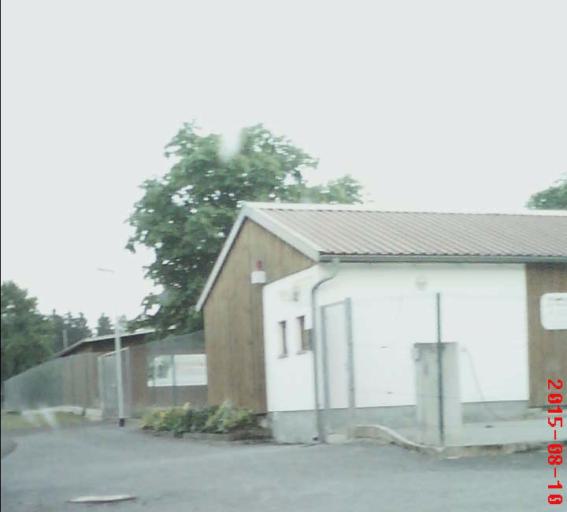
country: DE
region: Thuringia
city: Meiningen
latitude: 50.5676
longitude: 10.4426
